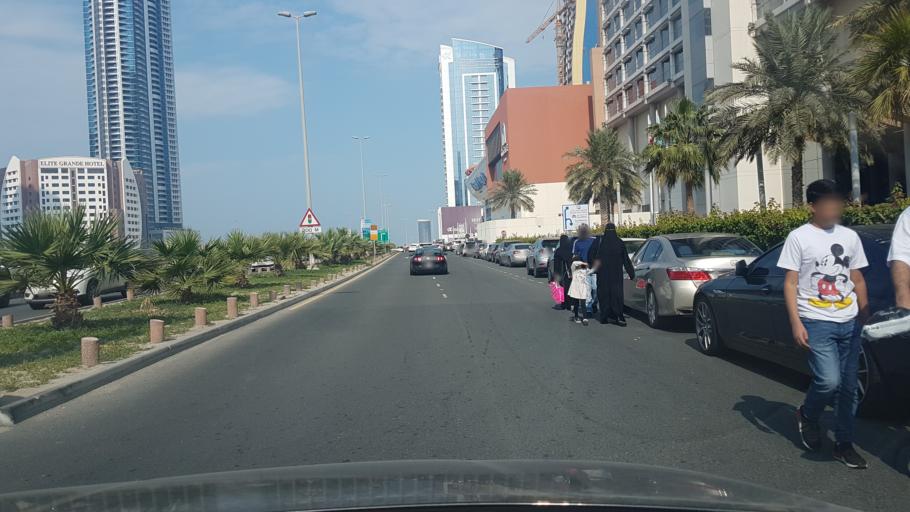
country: BH
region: Manama
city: Jidd Hafs
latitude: 26.2326
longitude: 50.5515
